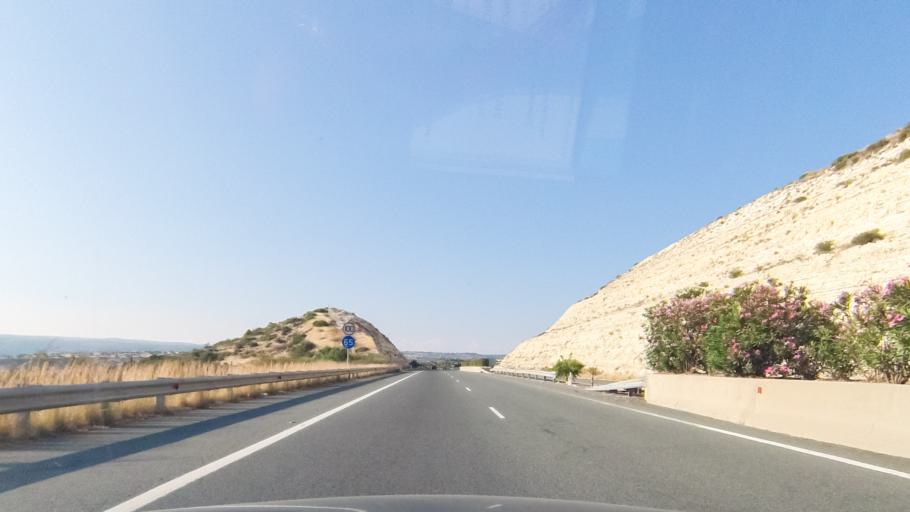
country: CY
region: Limassol
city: Sotira
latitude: 34.6828
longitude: 32.8055
